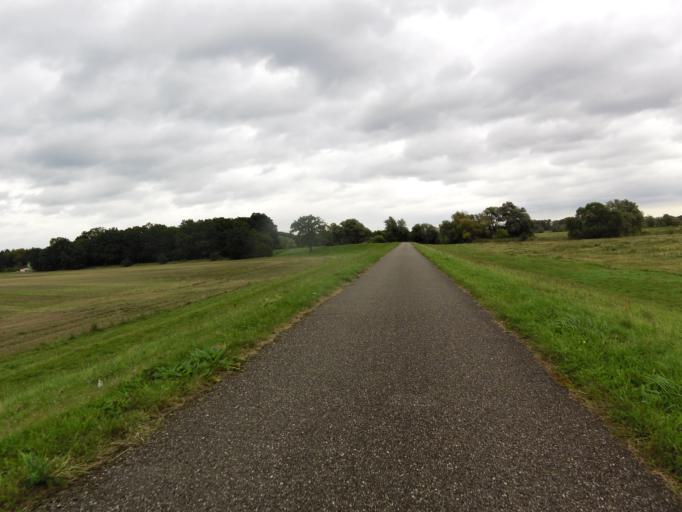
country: DE
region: Brandenburg
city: Bad Wilsnack
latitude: 52.8806
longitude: 11.9860
